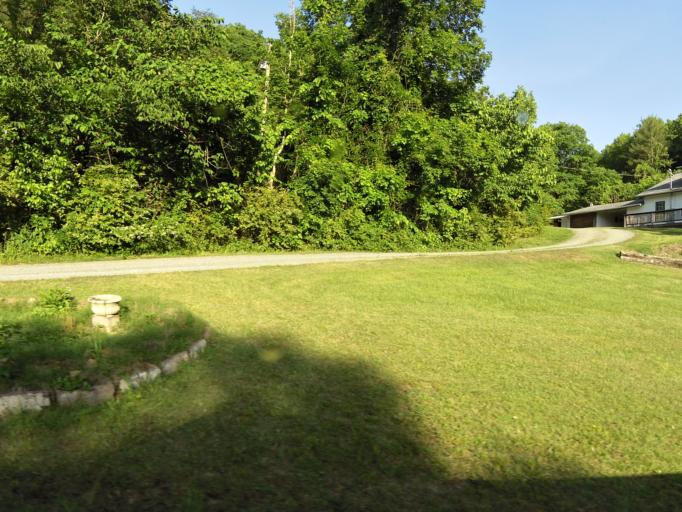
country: US
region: Tennessee
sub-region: Sevier County
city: Sevierville
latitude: 35.8552
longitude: -83.6298
